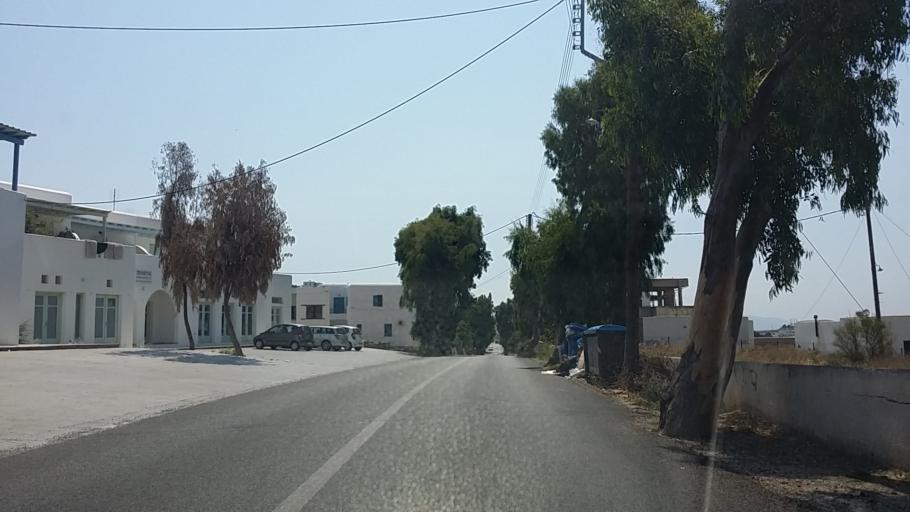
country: GR
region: South Aegean
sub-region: Nomos Kykladon
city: Naousa
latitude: 37.0432
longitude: 25.2466
